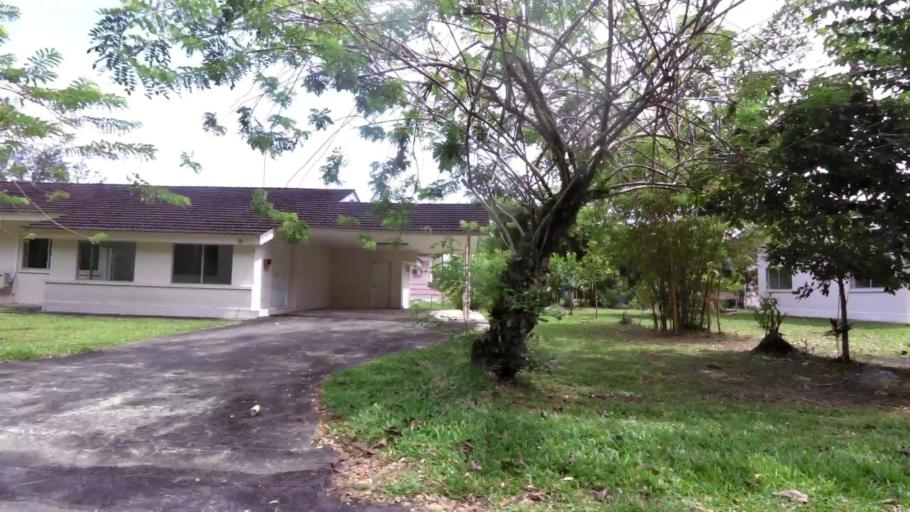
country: BN
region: Belait
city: Seria
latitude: 4.5982
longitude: 114.2900
